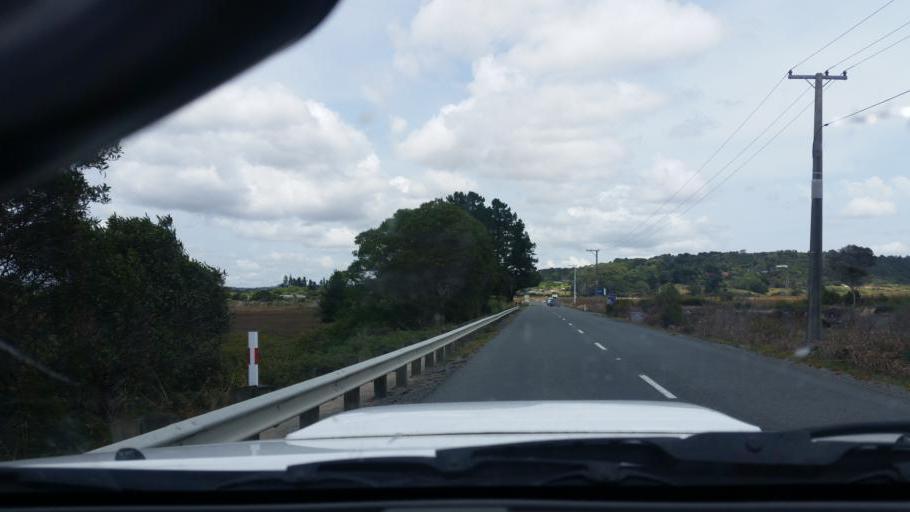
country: NZ
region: Auckland
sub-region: Auckland
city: Wellsford
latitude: -36.1098
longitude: 174.5780
